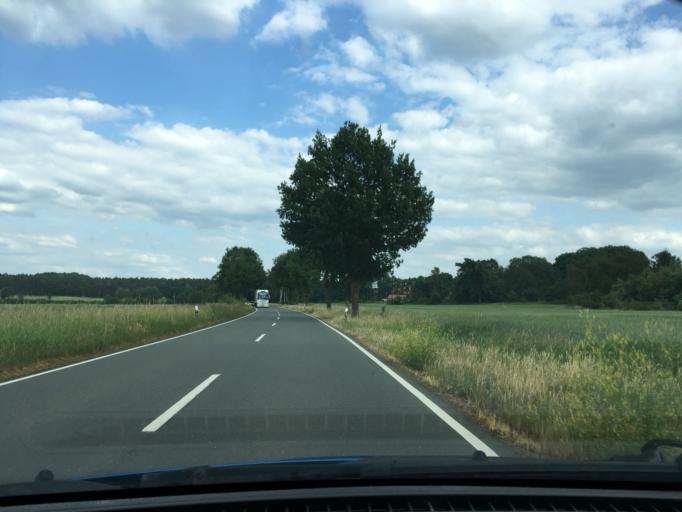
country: DE
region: Lower Saxony
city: Soderstorf
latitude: 53.1302
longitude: 10.1672
